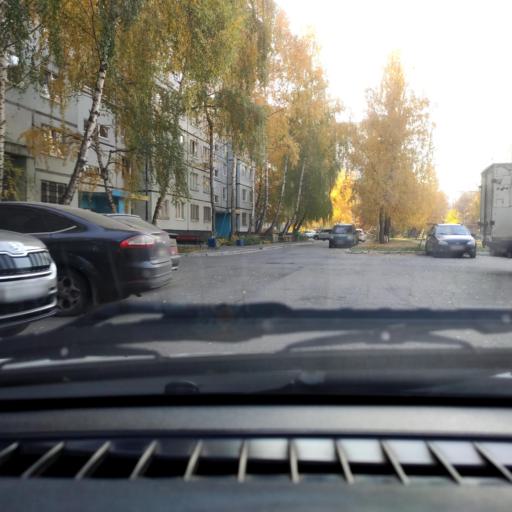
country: RU
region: Samara
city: Tol'yatti
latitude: 53.5087
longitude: 49.4494
